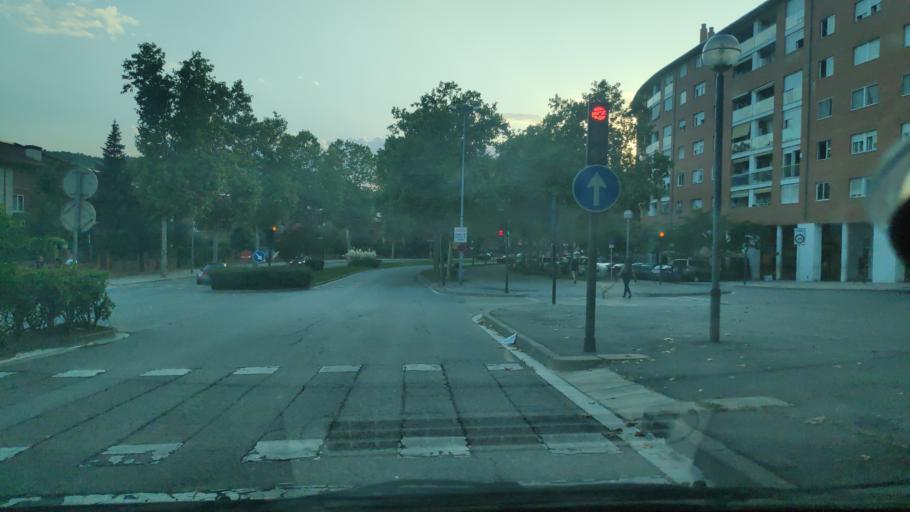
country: ES
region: Catalonia
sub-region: Provincia de Barcelona
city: Cerdanyola del Valles
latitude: 41.4830
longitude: 2.1471
